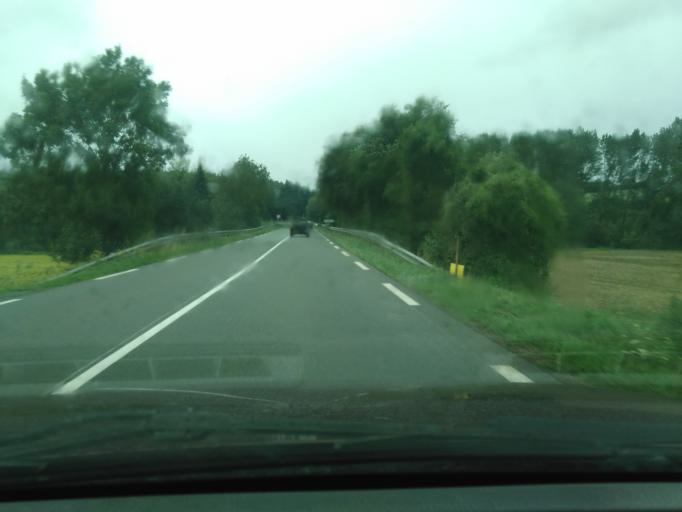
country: FR
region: Pays de la Loire
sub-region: Departement de la Vendee
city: Sainte-Hermine
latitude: 46.5874
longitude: -1.1167
